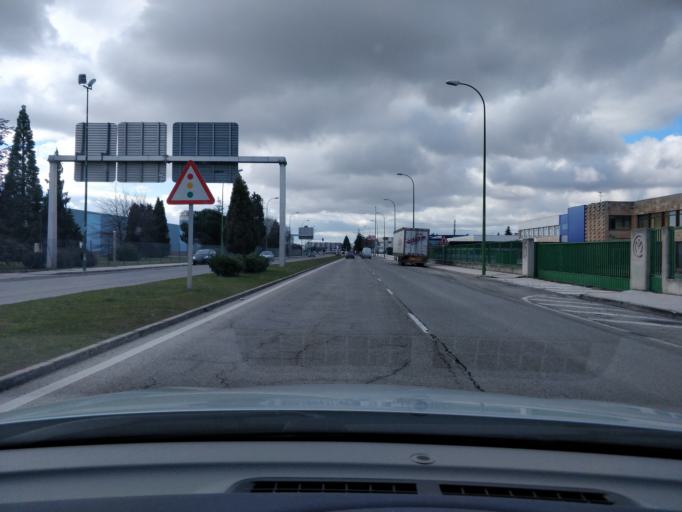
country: ES
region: Castille and Leon
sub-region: Provincia de Burgos
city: Burgos
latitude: 42.3603
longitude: -3.6439
